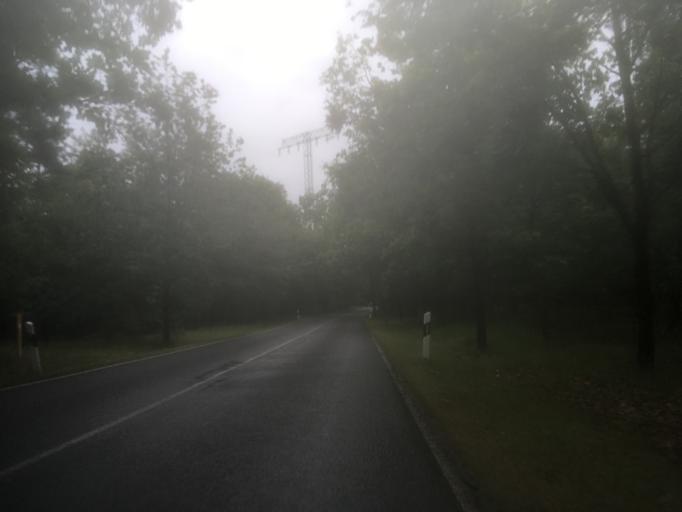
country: DE
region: Brandenburg
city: Zehdenick
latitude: 53.0447
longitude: 13.3193
